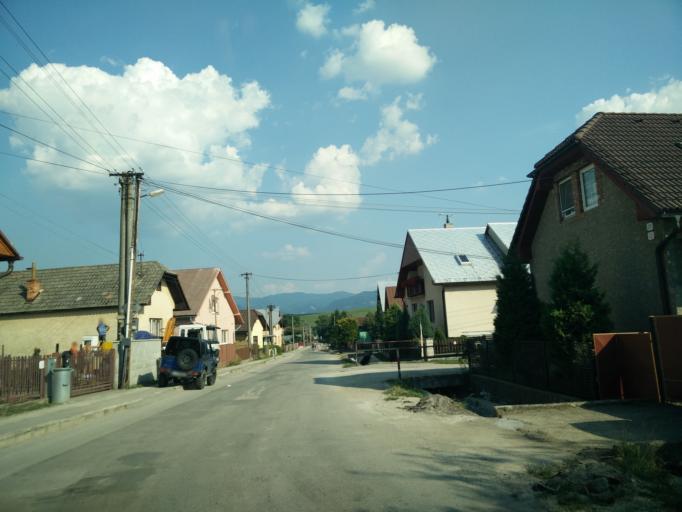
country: SK
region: Zilinsky
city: Rajec
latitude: 49.1210
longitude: 18.6469
